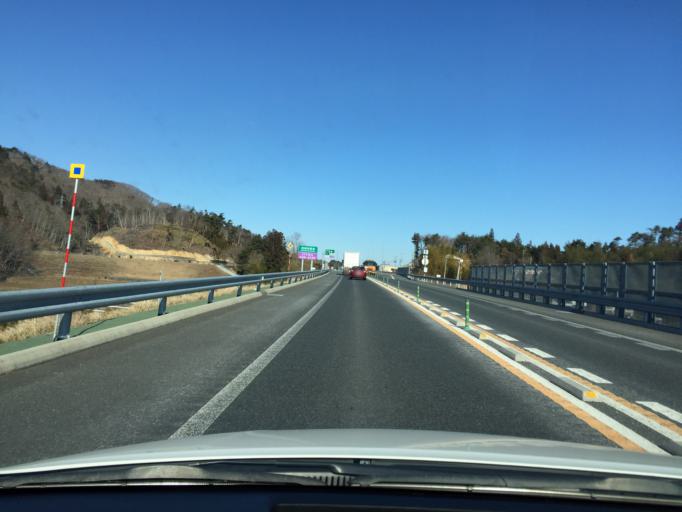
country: JP
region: Fukushima
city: Namie
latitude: 37.7100
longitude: 140.9223
